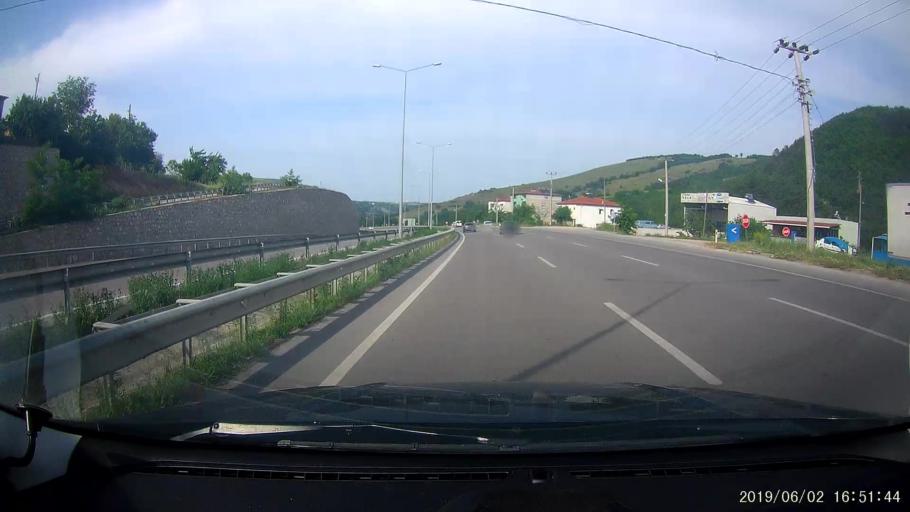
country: TR
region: Samsun
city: Samsun
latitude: 41.2775
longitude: 36.1872
